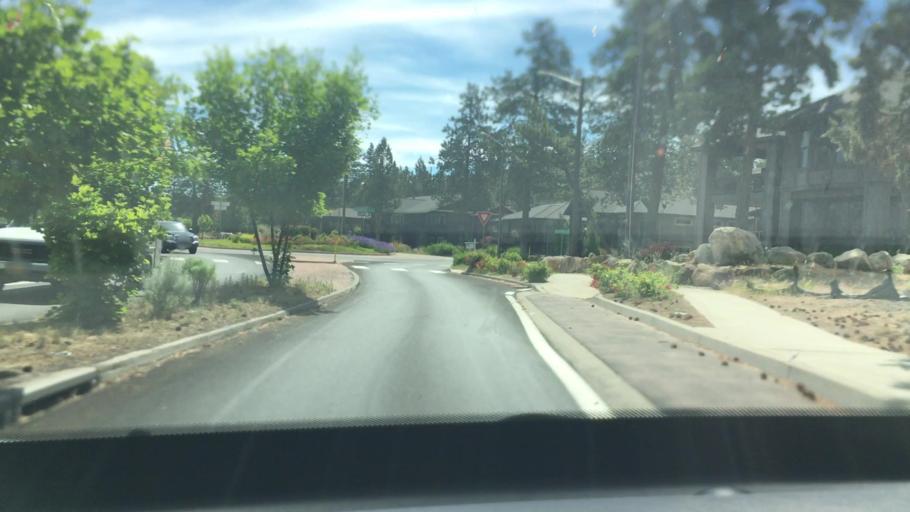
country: US
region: Oregon
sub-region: Deschutes County
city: Bend
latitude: 44.0406
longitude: -121.3225
